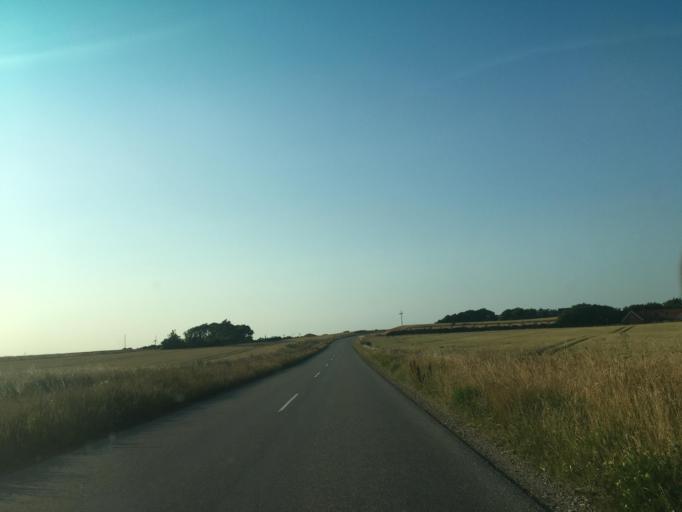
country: DK
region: North Denmark
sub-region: Thisted Kommune
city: Hurup
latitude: 56.7630
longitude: 8.4228
